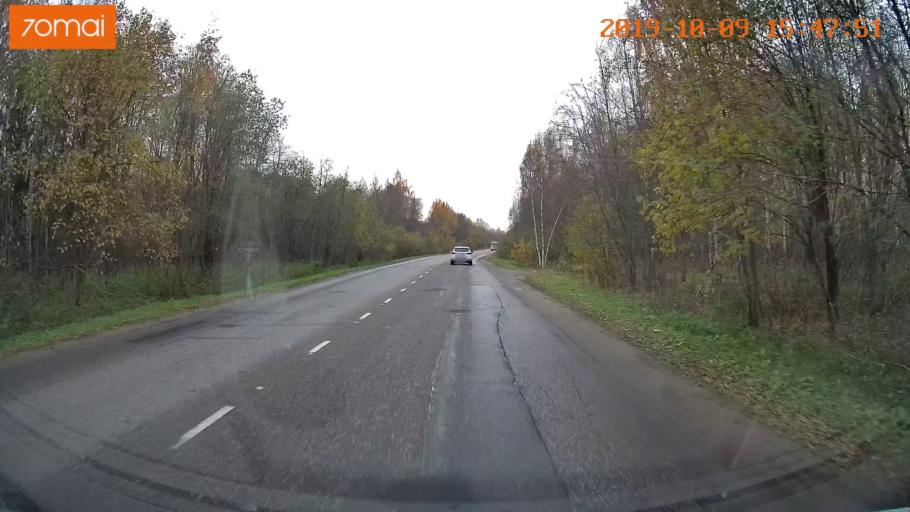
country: RU
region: Kostroma
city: Oktyabr'skiy
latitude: 57.8149
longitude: 41.0233
